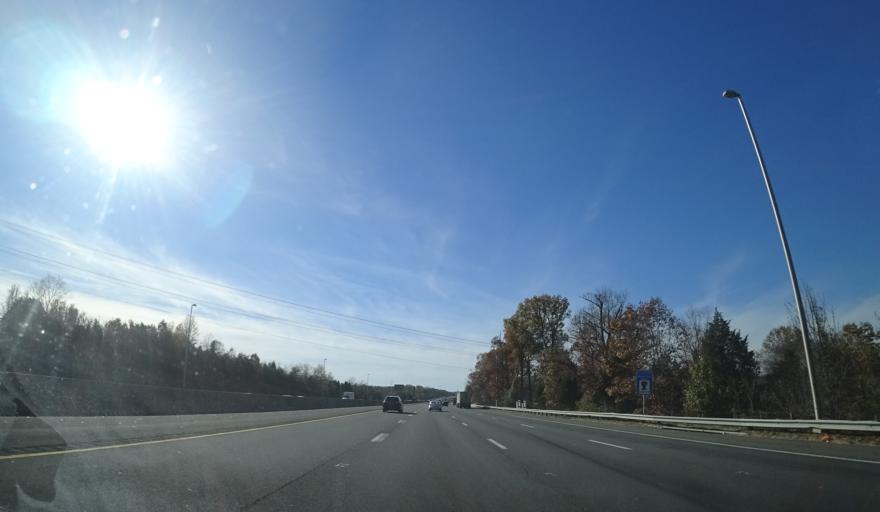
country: US
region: Virginia
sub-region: Prince William County
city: Yorkshire
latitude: 38.8192
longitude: -77.4670
